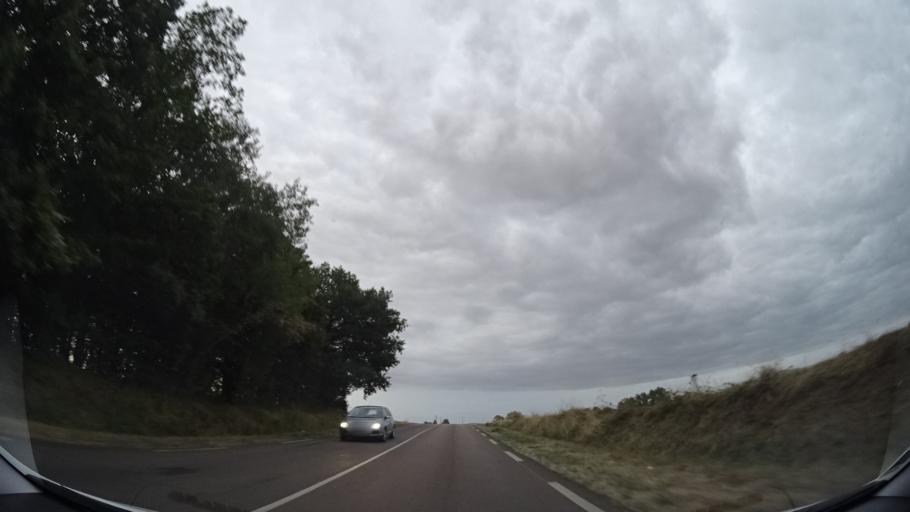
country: FR
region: Bourgogne
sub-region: Departement de l'Yonne
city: Charny
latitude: 47.9332
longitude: 3.1645
